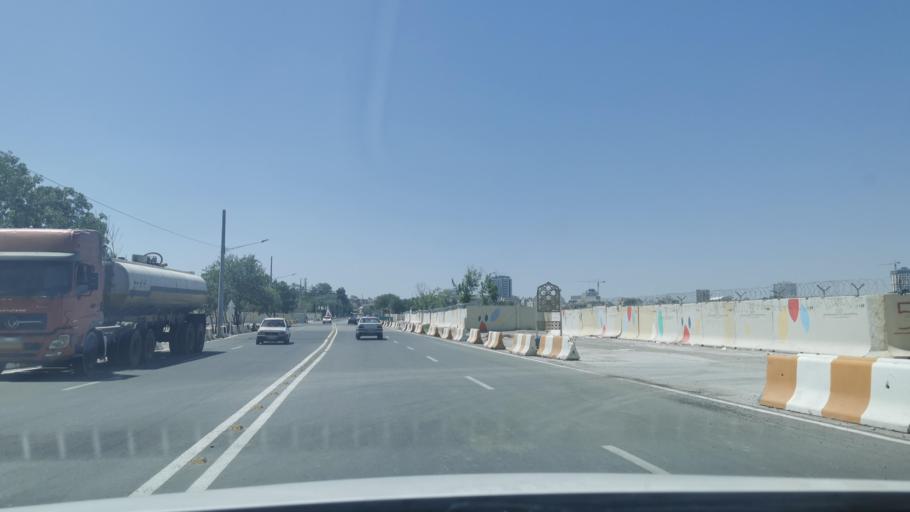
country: IR
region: Razavi Khorasan
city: Mashhad
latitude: 36.2734
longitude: 59.5834
